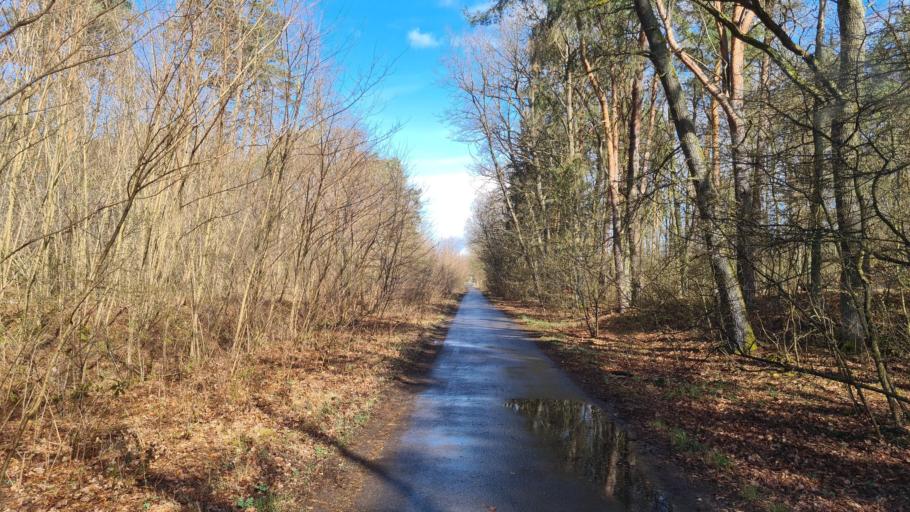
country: DE
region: Brandenburg
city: Altdobern
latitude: 51.7046
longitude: 14.0378
